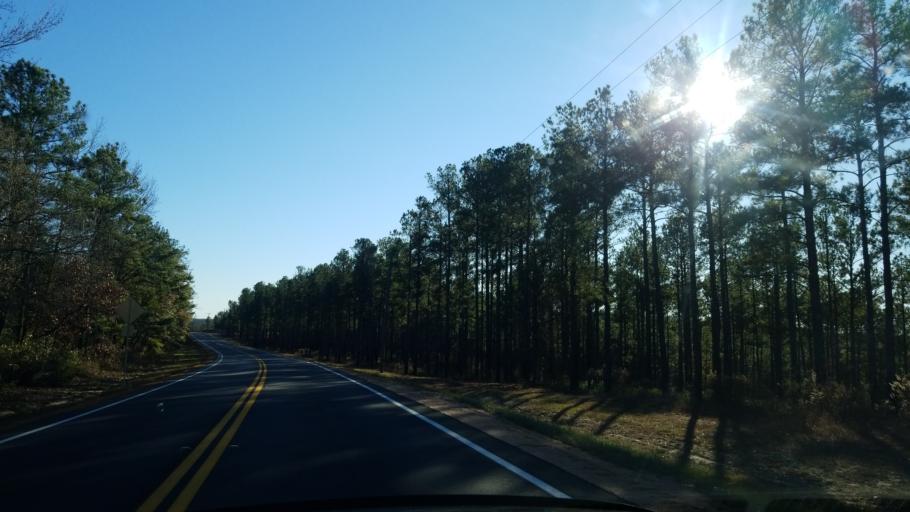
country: US
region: Georgia
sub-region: Talbot County
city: Talbotton
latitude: 32.5725
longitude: -84.5416
